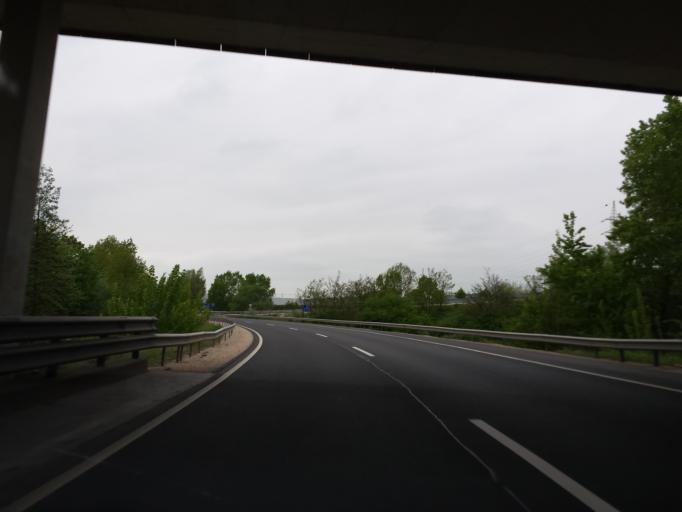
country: HU
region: Pest
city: Toeroekbalint
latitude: 47.4646
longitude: 18.8799
